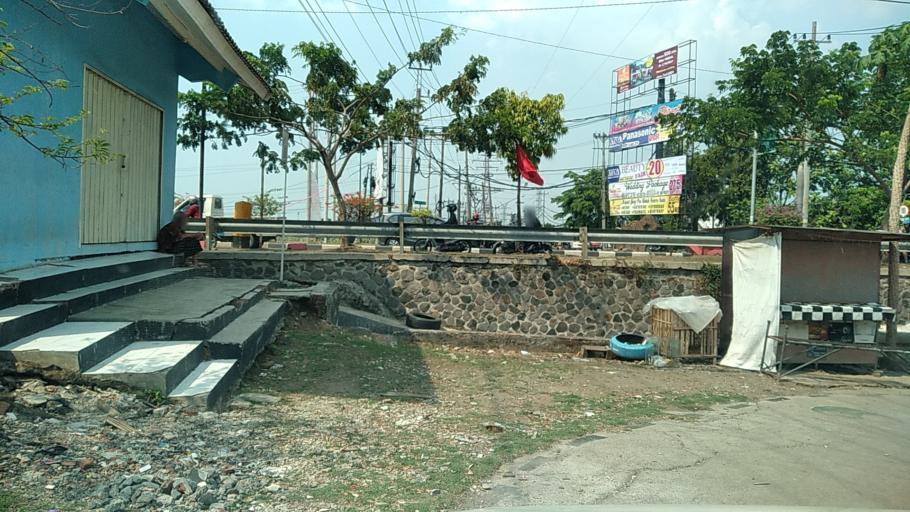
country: ID
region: Central Java
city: Semarang
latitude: -6.9975
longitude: 110.4391
